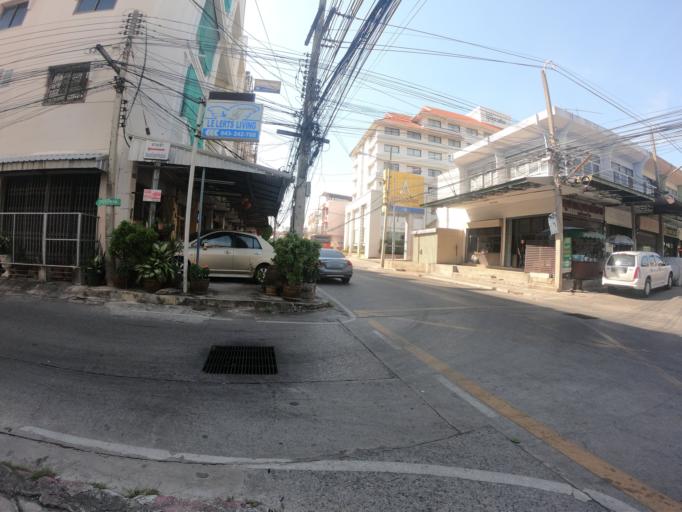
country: TH
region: Khon Kaen
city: Khon Kaen
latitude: 16.4368
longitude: 102.8334
